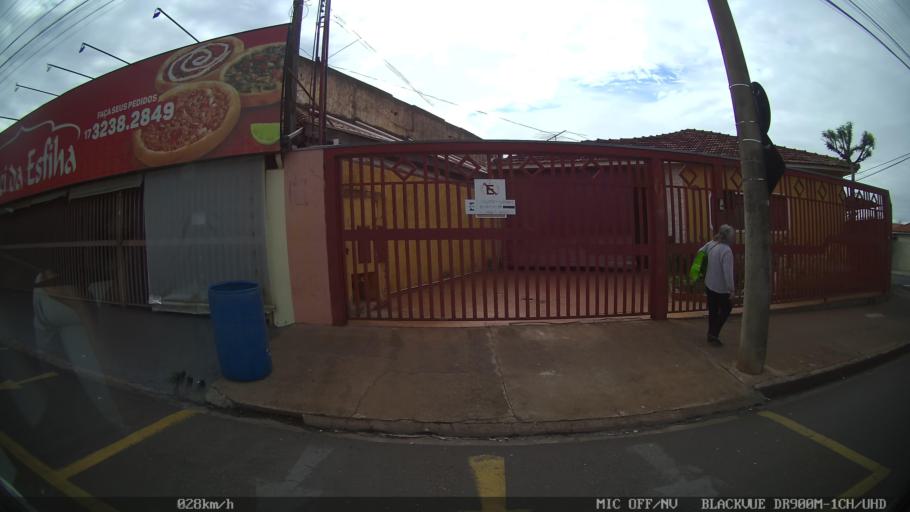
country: BR
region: Sao Paulo
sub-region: Sao Jose Do Rio Preto
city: Sao Jose do Rio Preto
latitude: -20.8205
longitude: -49.3538
